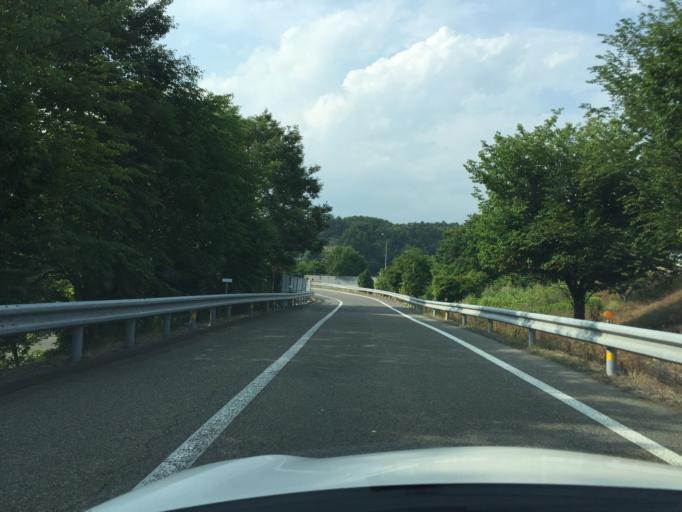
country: JP
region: Fukushima
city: Miharu
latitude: 37.4416
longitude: 140.4397
